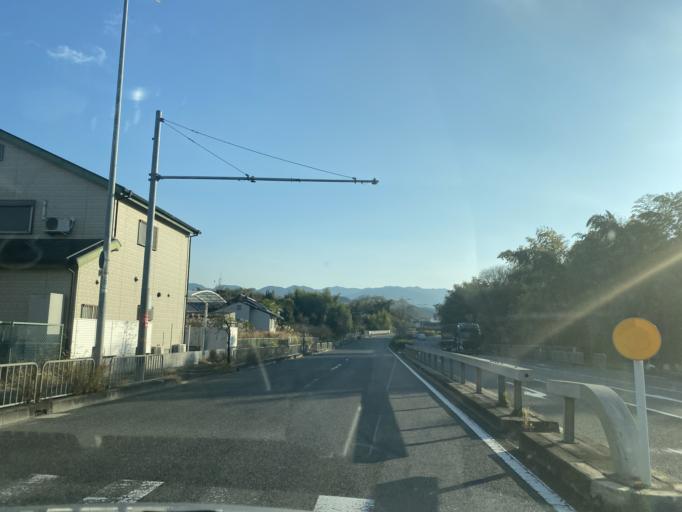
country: JP
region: Osaka
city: Izumi
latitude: 34.4264
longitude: 135.4402
